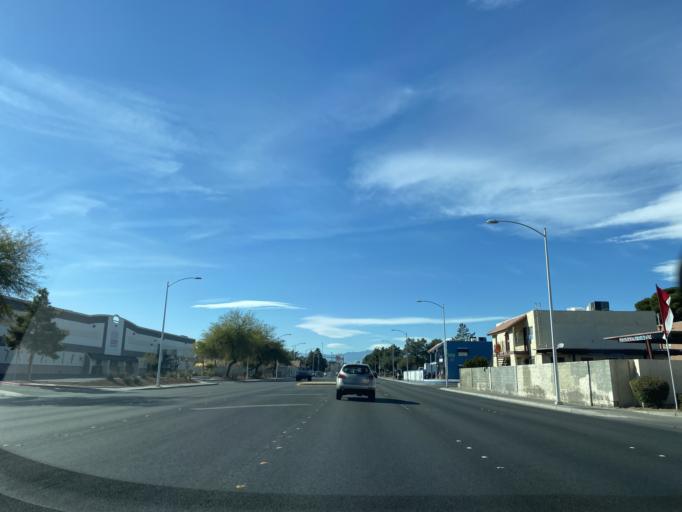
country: US
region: Nevada
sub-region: Clark County
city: Sunrise Manor
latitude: 36.1735
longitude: -115.0857
